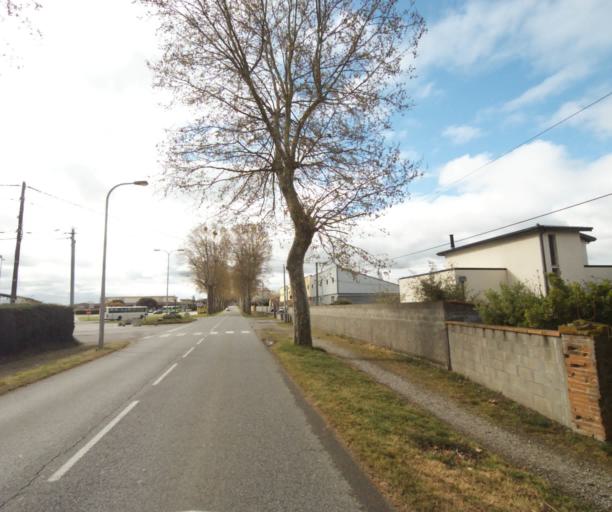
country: FR
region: Midi-Pyrenees
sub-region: Departement de l'Ariege
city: Saverdun
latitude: 43.2422
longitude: 1.5711
